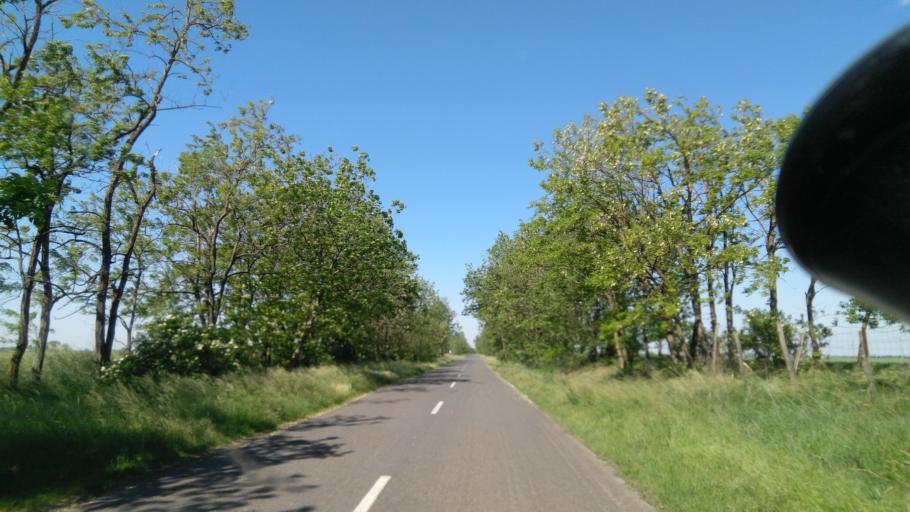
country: HU
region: Bekes
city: Kevermes
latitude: 46.4259
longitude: 21.1538
